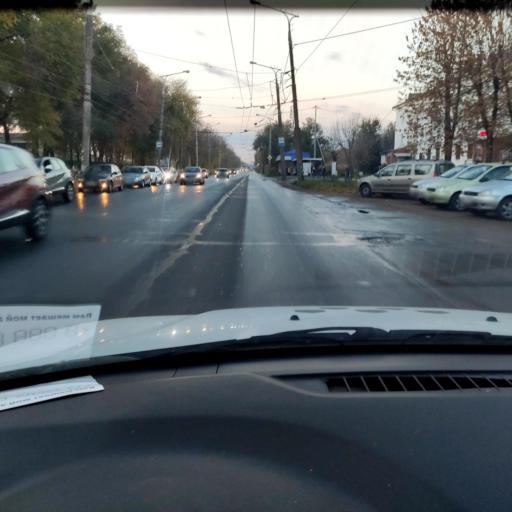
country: RU
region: Samara
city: Tol'yatti
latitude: 53.5410
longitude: 49.4433
